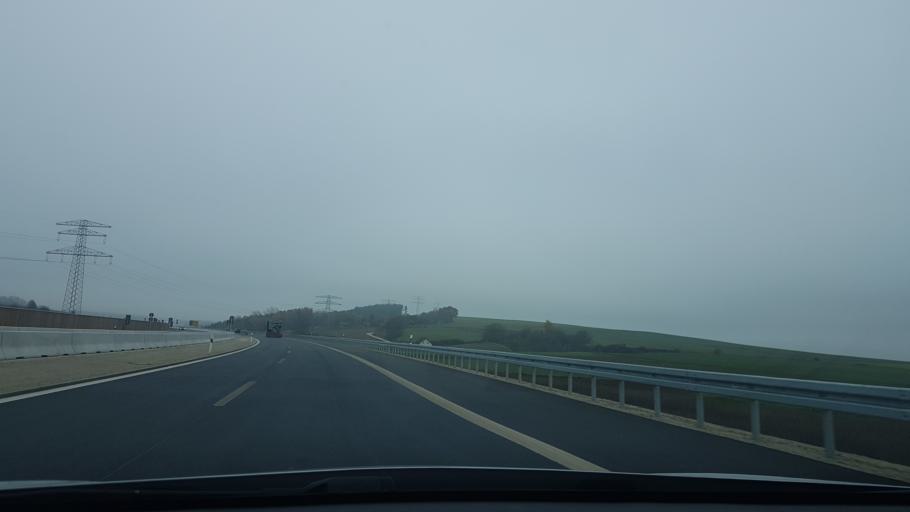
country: DE
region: Bavaria
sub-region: Lower Bavaria
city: Essenbach
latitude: 48.6197
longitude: 12.2281
